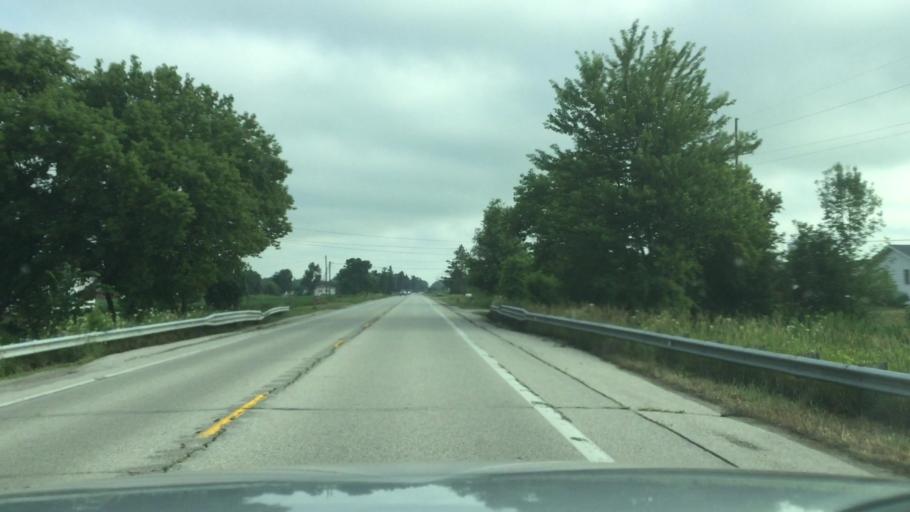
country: US
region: Michigan
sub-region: Saginaw County
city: Frankenmuth
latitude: 43.2709
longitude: -83.7357
